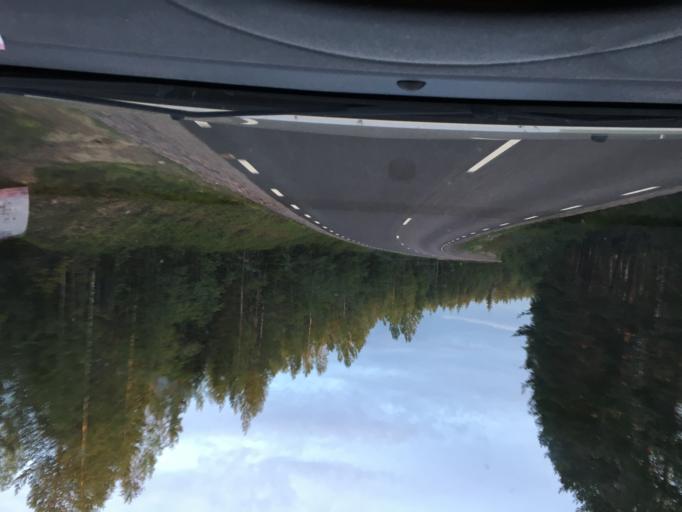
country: SE
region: Norrbotten
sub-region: Lulea Kommun
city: Ranea
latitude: 66.0484
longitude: 22.2358
